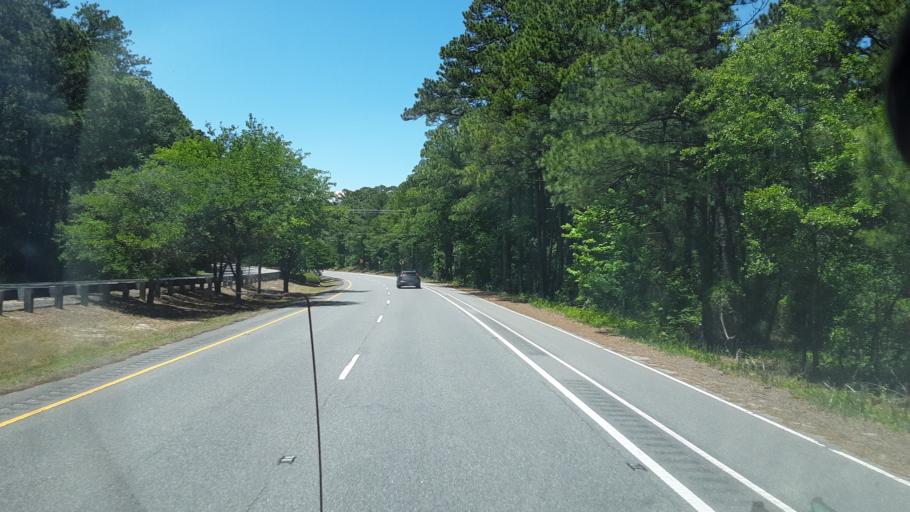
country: US
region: Virginia
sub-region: City of Virginia Beach
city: Virginia Beach
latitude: 36.9208
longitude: -76.0409
